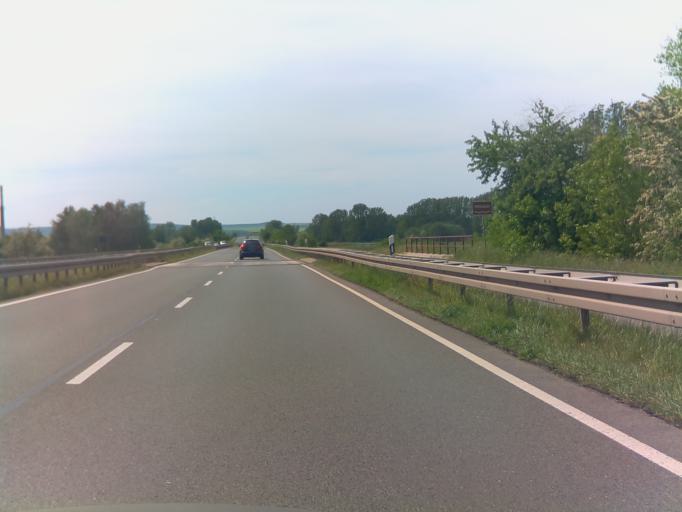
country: DE
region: Saxony-Anhalt
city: Egeln
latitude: 51.9491
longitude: 11.4272
